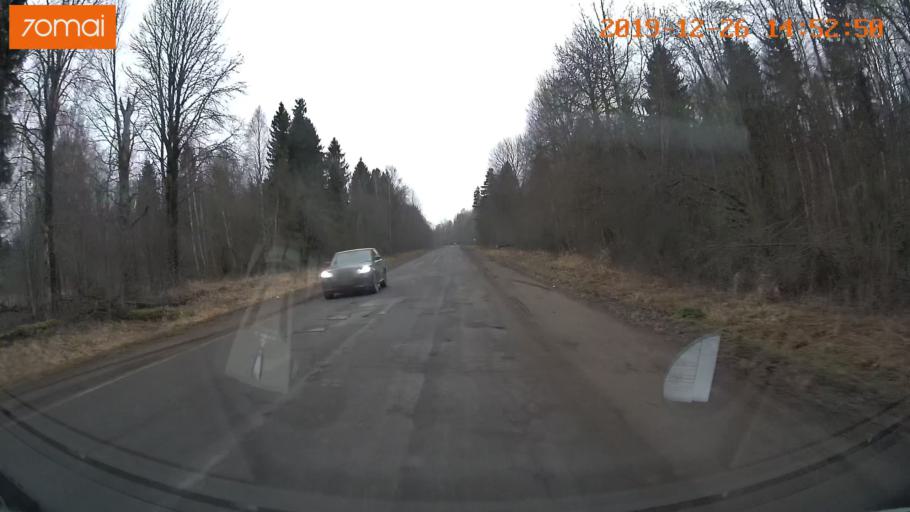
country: RU
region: Jaroslavl
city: Rybinsk
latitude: 58.3191
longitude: 38.8946
